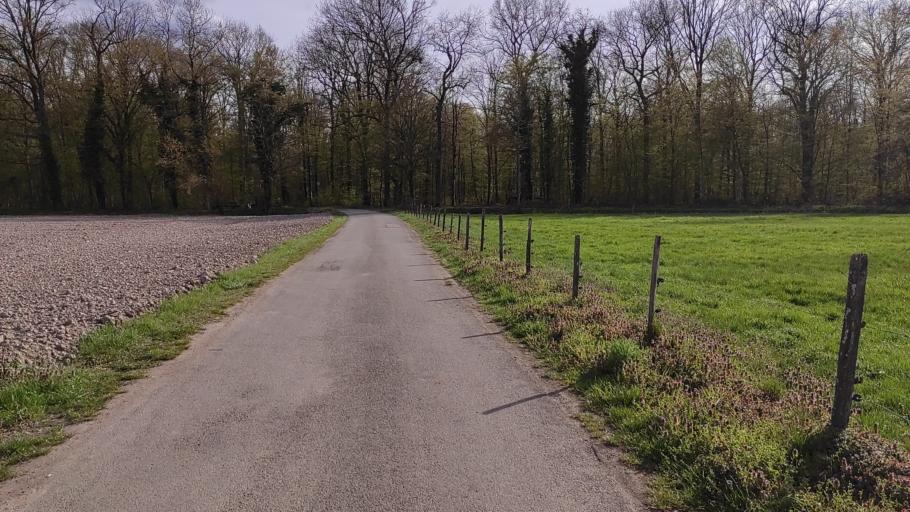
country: DE
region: Baden-Wuerttemberg
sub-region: Freiburg Region
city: Schallstadt
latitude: 47.9886
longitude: 7.7597
